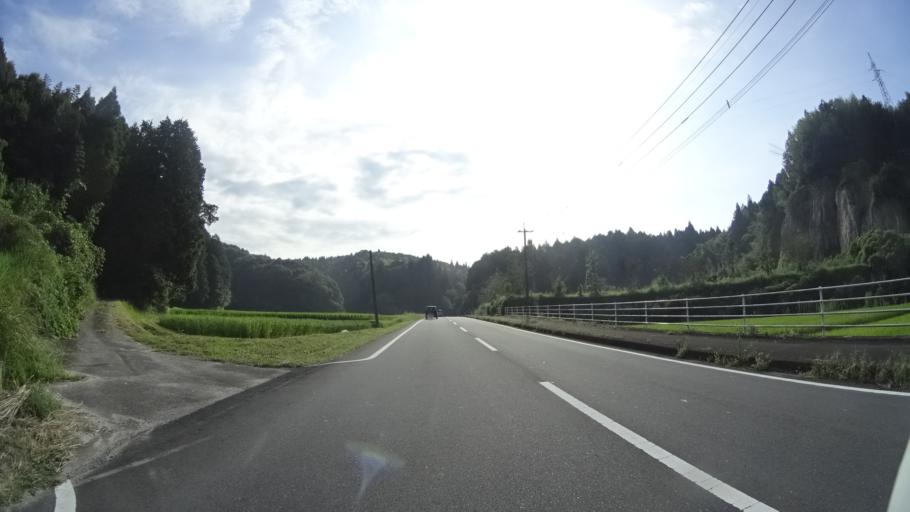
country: JP
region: Kagoshima
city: Okuchi-shinohara
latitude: 32.0181
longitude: 130.6241
